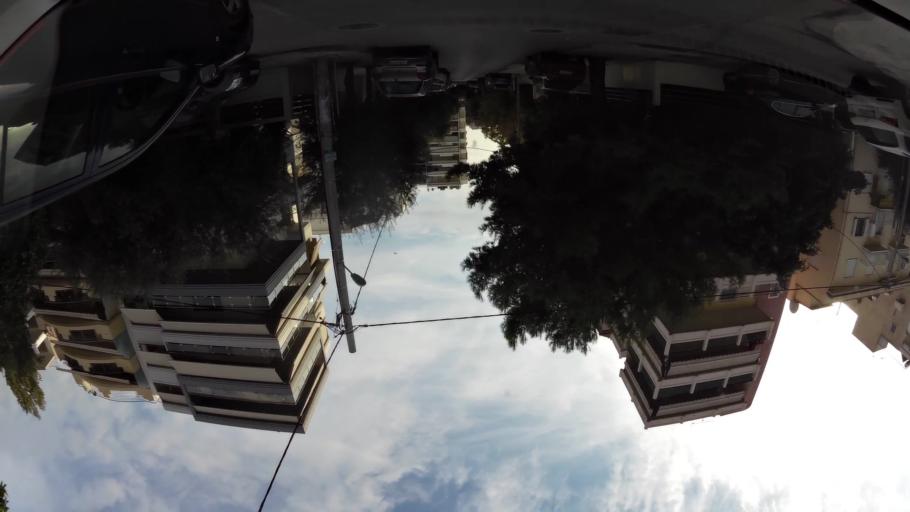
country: GR
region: Attica
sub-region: Nomarchia Athinas
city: Palaio Faliro
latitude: 37.9344
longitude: 23.6977
